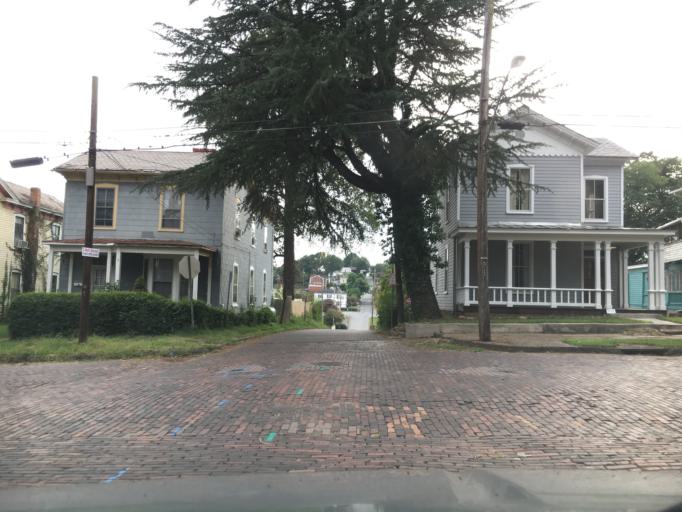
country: US
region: Virginia
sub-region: City of Lynchburg
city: Lynchburg
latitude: 37.4165
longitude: -79.1504
